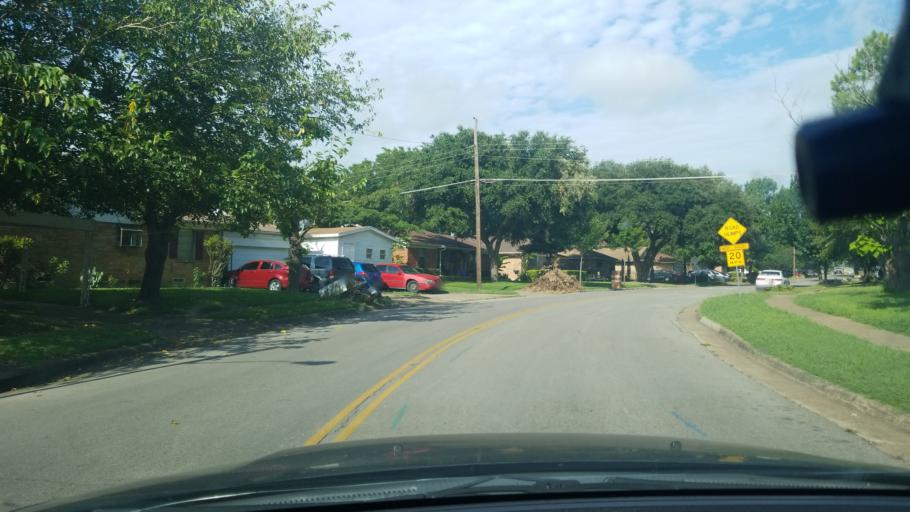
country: US
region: Texas
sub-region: Dallas County
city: Balch Springs
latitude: 32.7436
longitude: -96.6706
